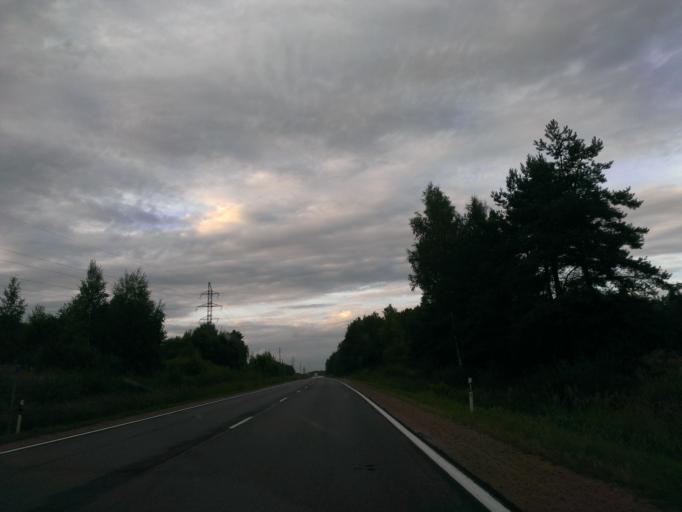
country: LV
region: Salaspils
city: Salaspils
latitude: 56.8674
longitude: 24.4069
